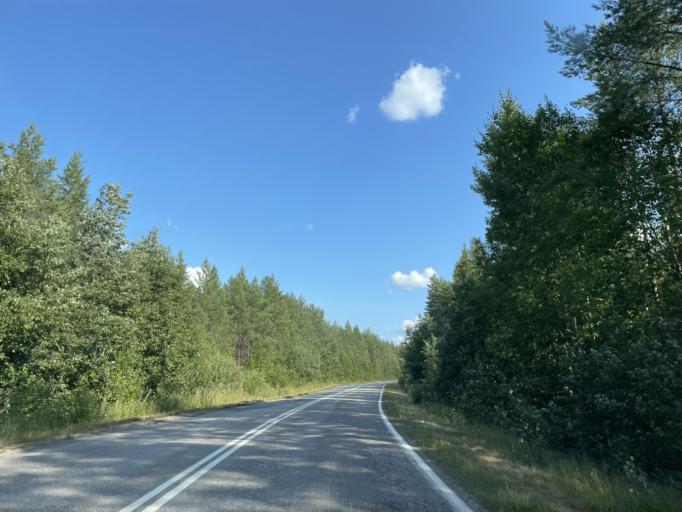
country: FI
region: Central Finland
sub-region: Saarijaervi-Viitasaari
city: Pihtipudas
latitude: 63.3658
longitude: 25.7101
